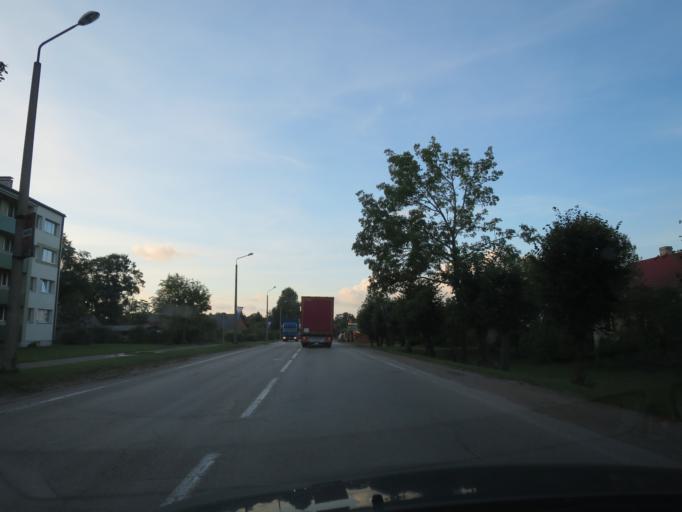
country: LV
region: Salacgrivas
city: Salacgriva
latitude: 57.7576
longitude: 24.3612
